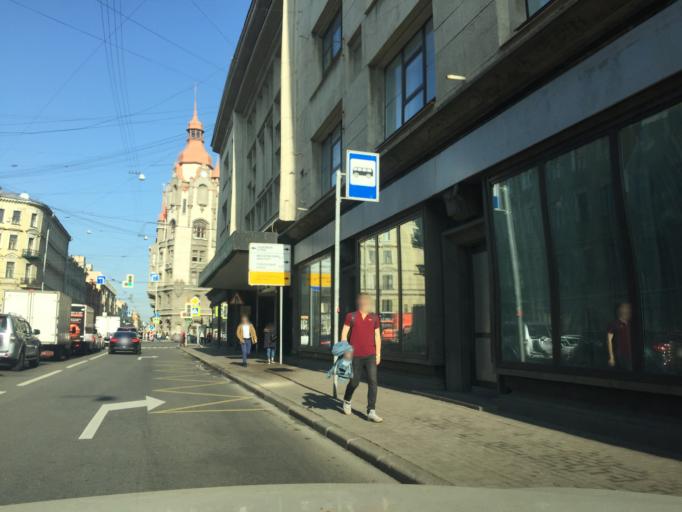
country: RU
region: St.-Petersburg
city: Saint Petersburg
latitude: 59.9218
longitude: 30.3081
